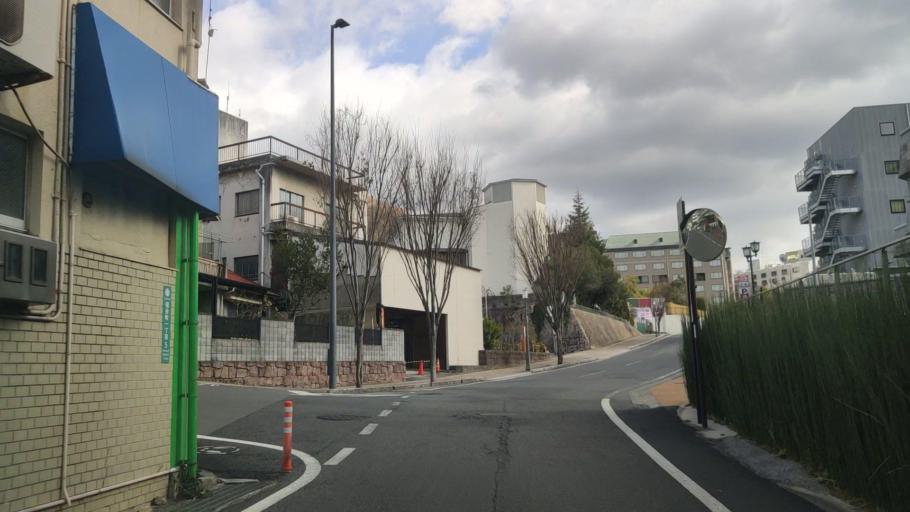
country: JP
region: Ehime
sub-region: Shikoku-chuo Shi
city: Matsuyama
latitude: 33.8544
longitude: 132.7845
